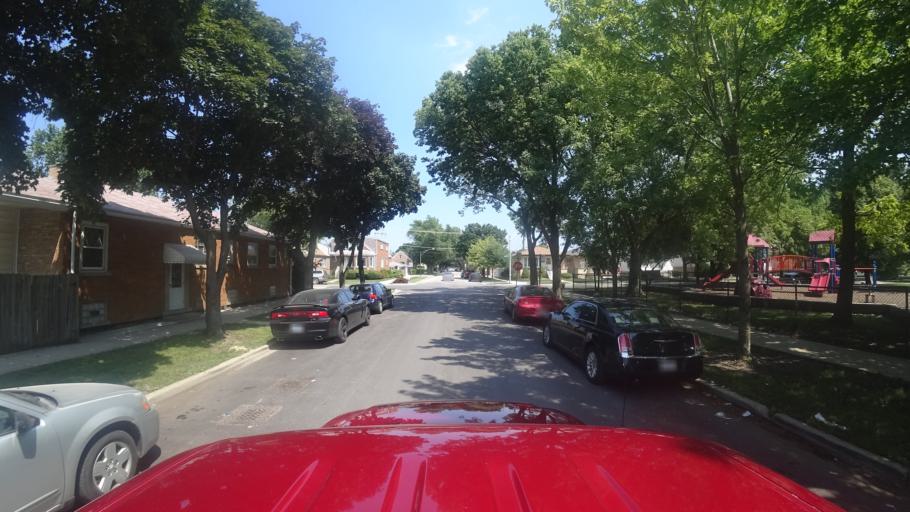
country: US
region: Illinois
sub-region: Cook County
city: Cicero
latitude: 41.7949
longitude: -87.7323
